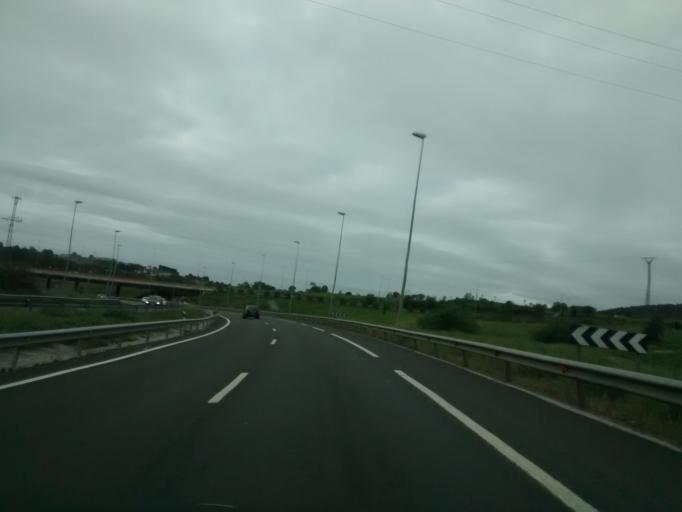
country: ES
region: Cantabria
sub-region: Provincia de Cantabria
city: Torrelavega
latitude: 43.3442
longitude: -4.0270
